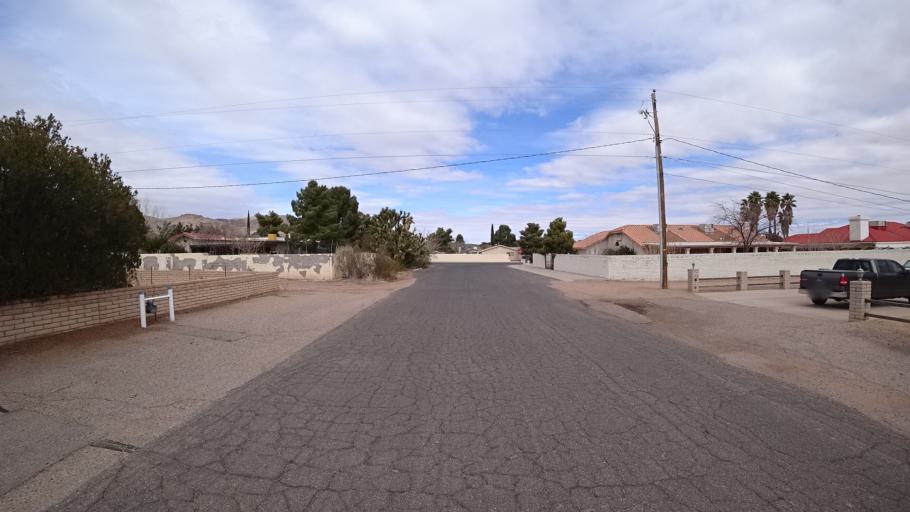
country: US
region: Arizona
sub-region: Mohave County
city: New Kingman-Butler
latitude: 35.2330
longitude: -114.0435
